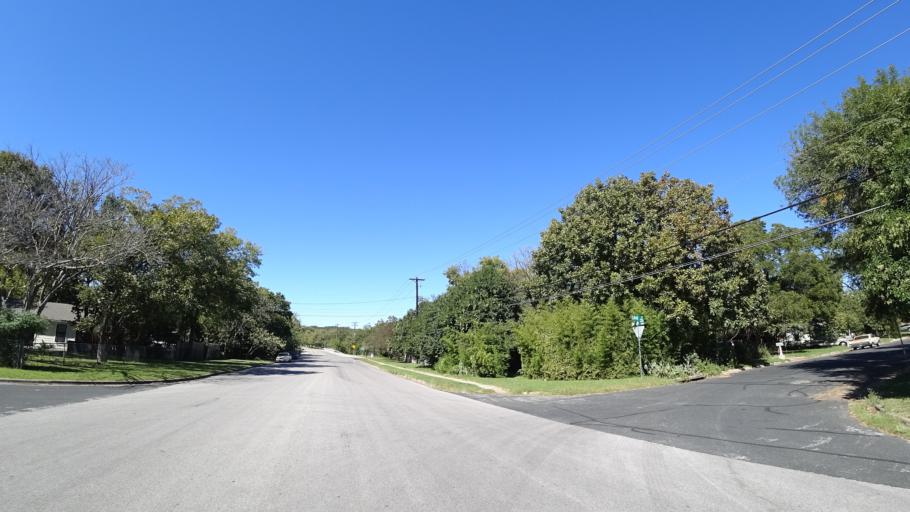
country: US
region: Texas
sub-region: Travis County
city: Austin
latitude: 30.2362
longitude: -97.7700
